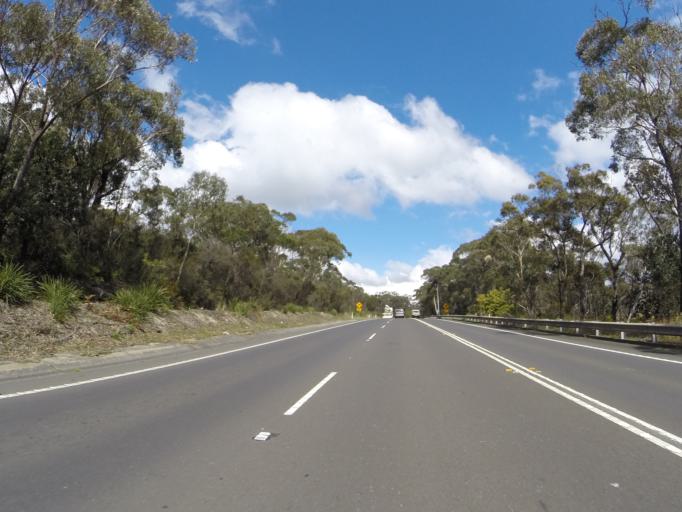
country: AU
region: New South Wales
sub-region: Wollongong
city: Mount Ousley
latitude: -34.3742
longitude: 150.8431
